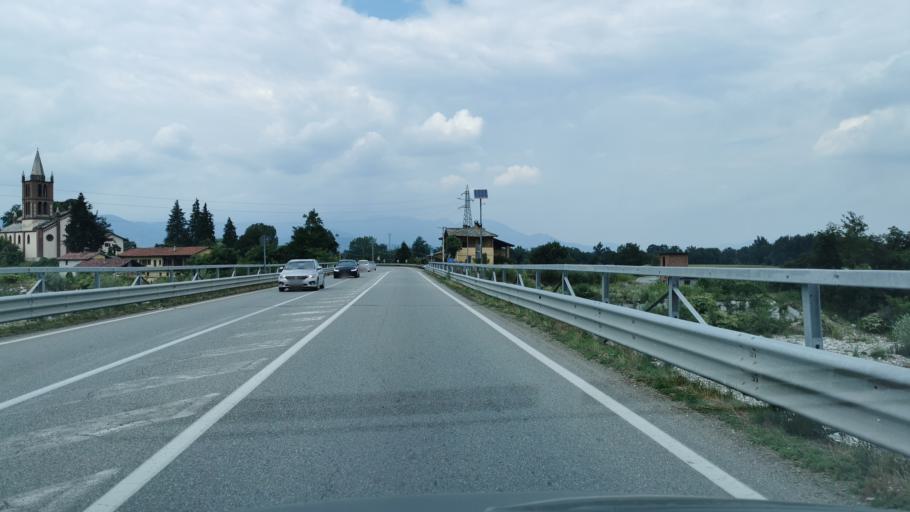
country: IT
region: Piedmont
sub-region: Provincia di Torino
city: Garzigliana
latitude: 44.8286
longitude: 7.3681
